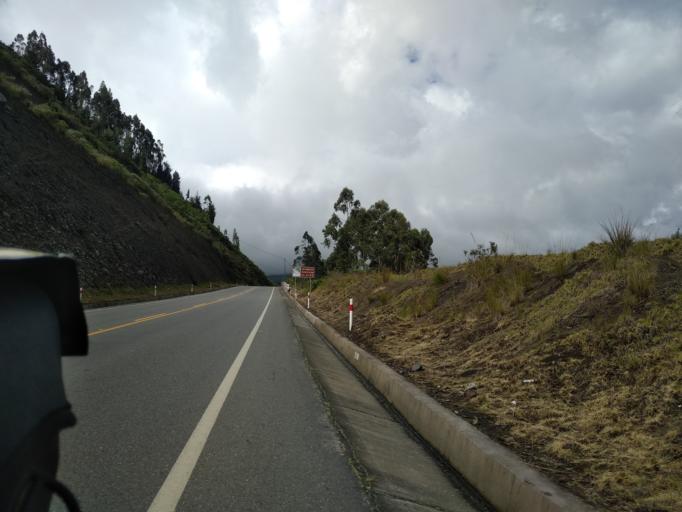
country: EC
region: Tungurahua
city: Banos
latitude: -1.4945
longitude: -78.5218
